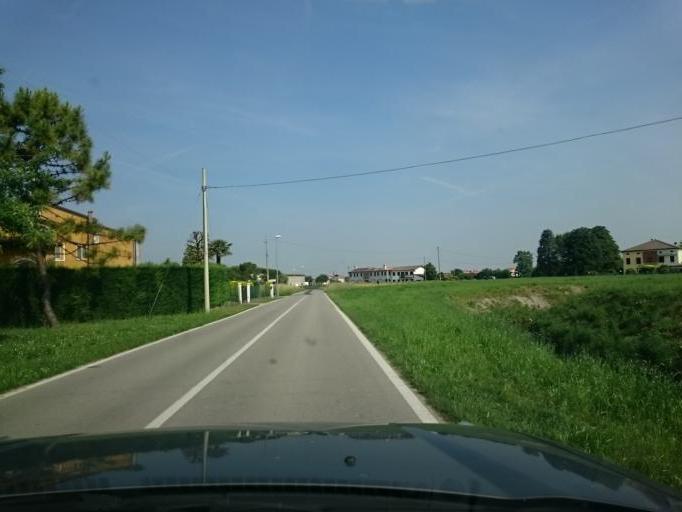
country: IT
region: Veneto
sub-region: Provincia di Padova
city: Ponte San Nicolo
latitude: 45.3592
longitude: 11.9130
